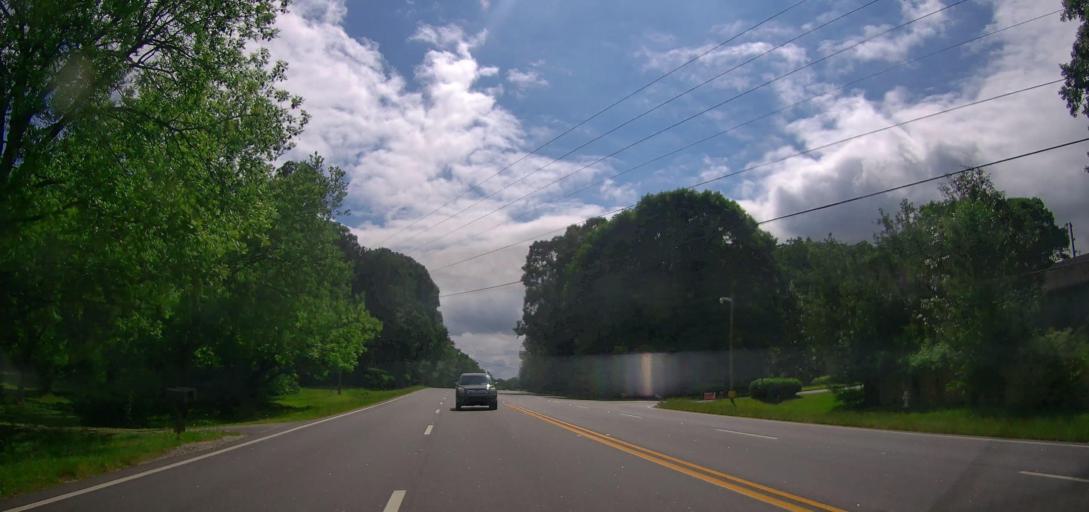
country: US
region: Georgia
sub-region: Rockdale County
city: Conyers
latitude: 33.6280
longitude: -84.0416
